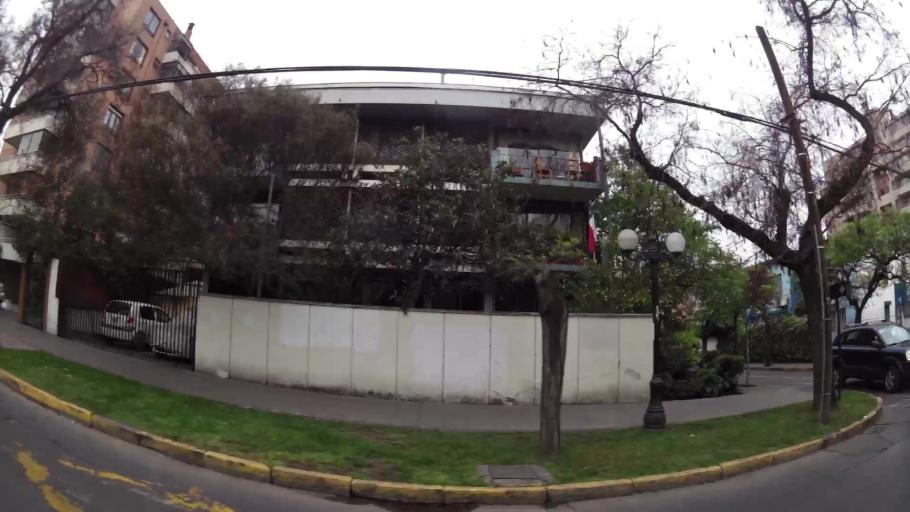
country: CL
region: Santiago Metropolitan
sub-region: Provincia de Santiago
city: Santiago
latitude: -33.4362
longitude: -70.6191
